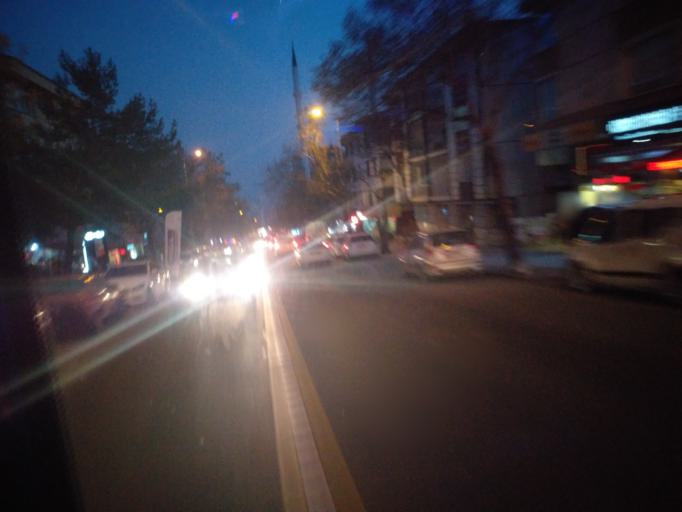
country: TR
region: Ankara
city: Ankara
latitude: 39.9753
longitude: 32.8411
